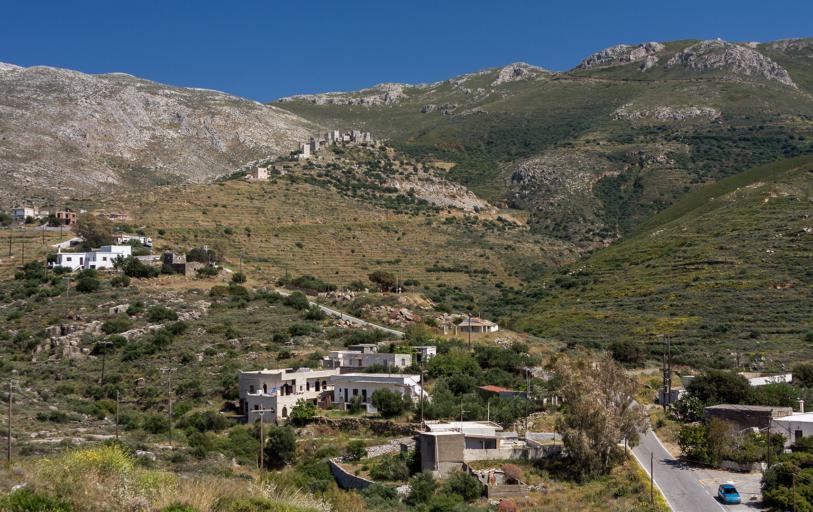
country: GR
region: Peloponnese
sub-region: Nomos Lakonias
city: Gytheio
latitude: 36.4563
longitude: 22.4511
